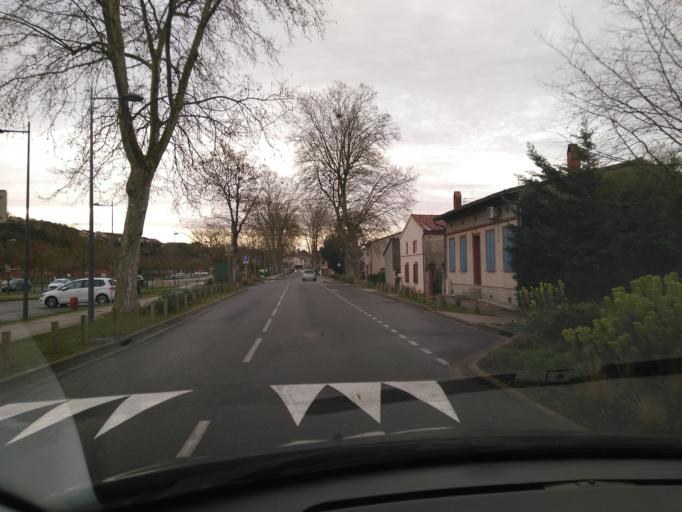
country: FR
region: Midi-Pyrenees
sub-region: Departement de la Haute-Garonne
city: Castelnau-d'Estretefonds
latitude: 43.7855
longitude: 1.3545
